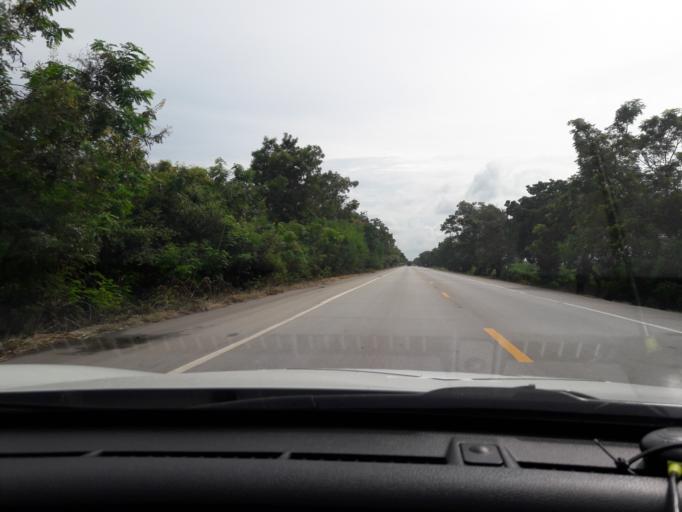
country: TH
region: Nakhon Sawan
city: Phai Sali
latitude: 15.5040
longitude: 100.5419
